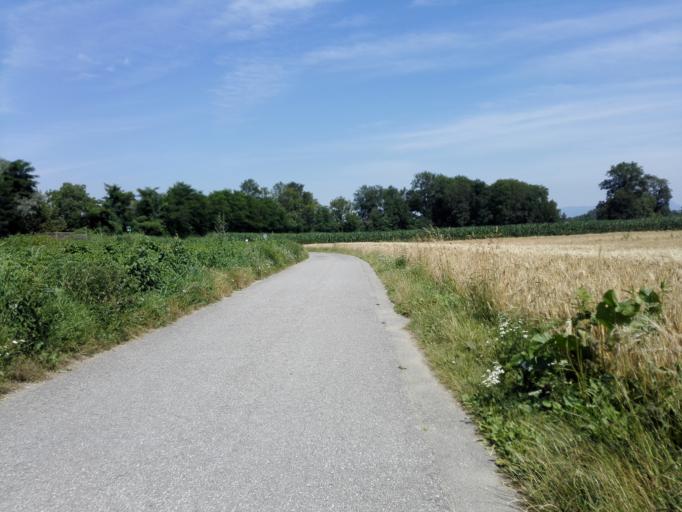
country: AT
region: Styria
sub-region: Politischer Bezirk Graz-Umgebung
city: Feldkirchen bei Graz
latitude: 47.0071
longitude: 15.4530
